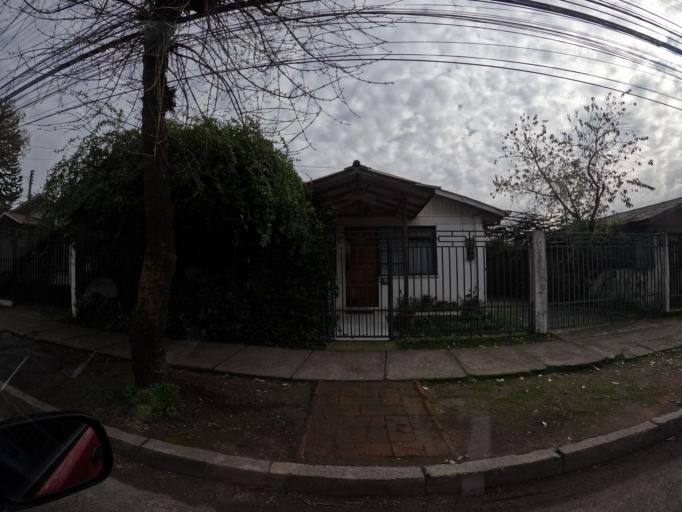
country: CL
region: Maule
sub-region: Provincia de Linares
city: Linares
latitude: -35.8375
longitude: -71.6026
